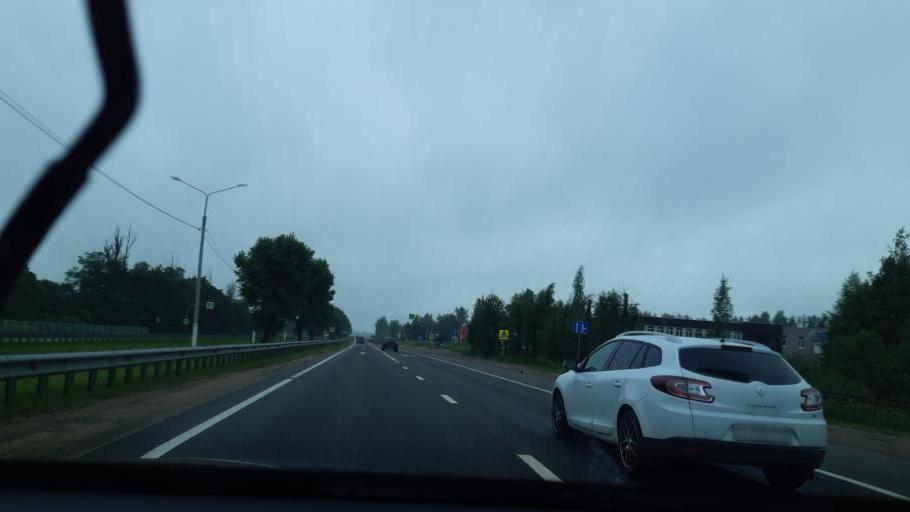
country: RU
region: Smolensk
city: Talashkino
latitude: 54.6842
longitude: 32.1376
